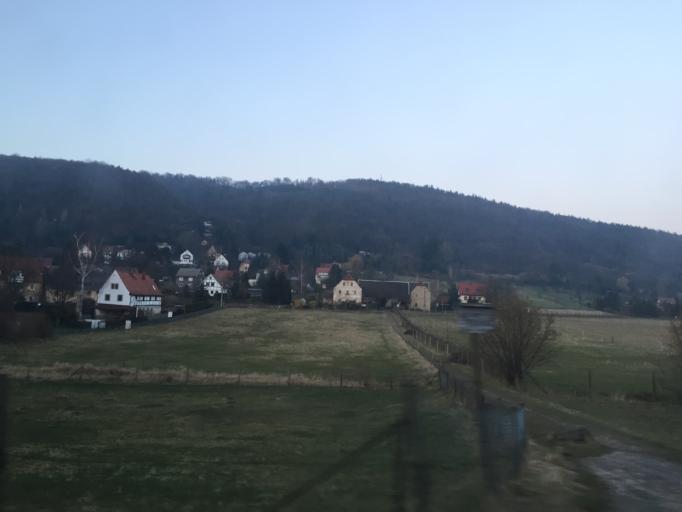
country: DE
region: Saxony
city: Heidenau
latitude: 51.0021
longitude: 13.8964
